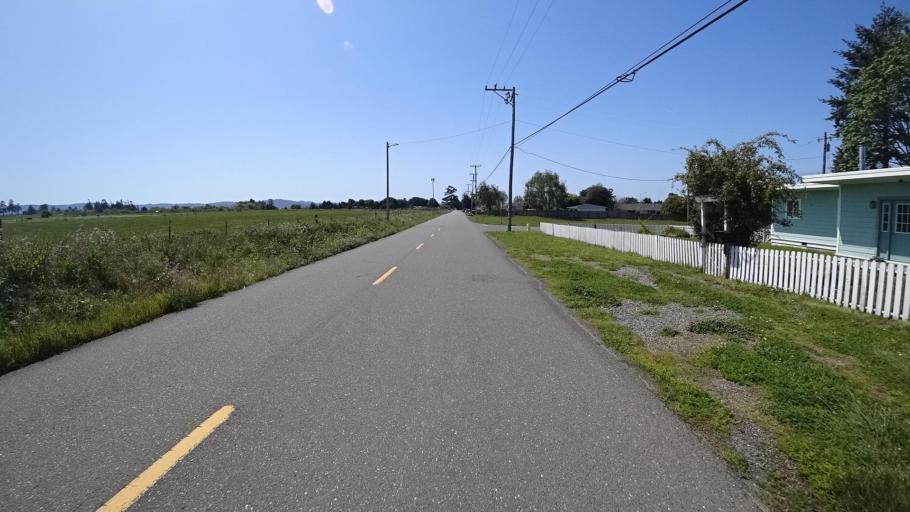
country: US
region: California
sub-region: Humboldt County
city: Hydesville
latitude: 40.5630
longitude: -124.1345
